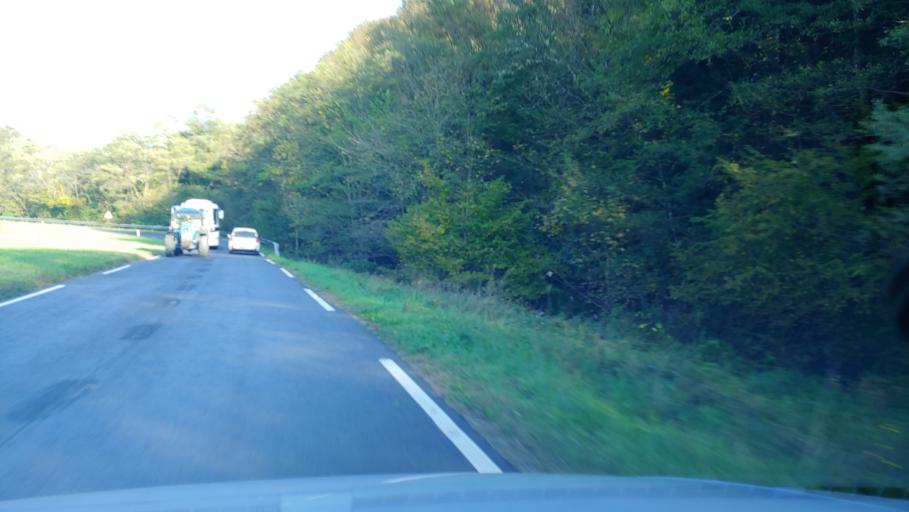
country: SI
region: Vipava
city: Vipava
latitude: 45.8125
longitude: 13.8976
